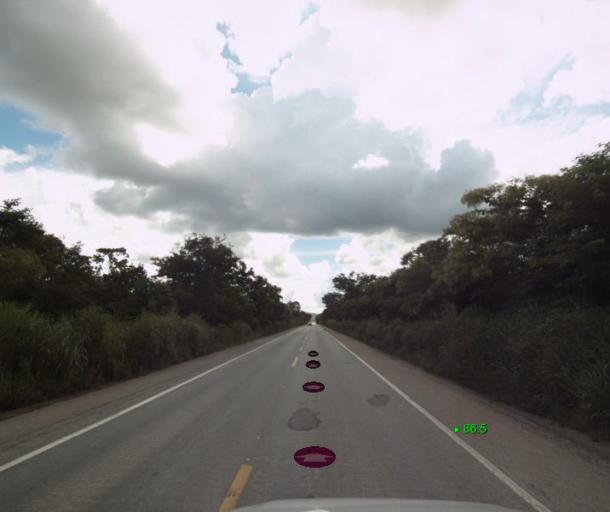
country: BR
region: Goias
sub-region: Porangatu
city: Porangatu
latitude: -13.5540
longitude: -49.0801
